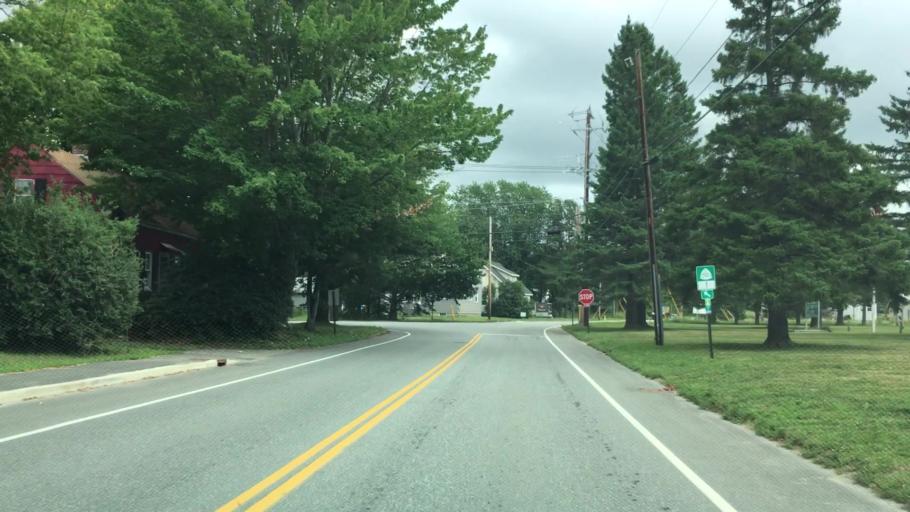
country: US
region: Maine
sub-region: Penobscot County
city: Brewer
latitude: 44.7672
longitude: -68.7739
